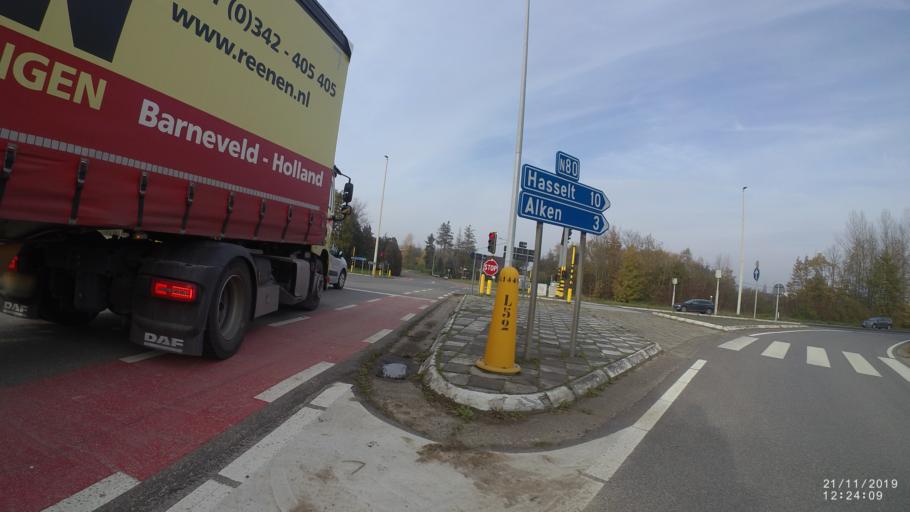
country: BE
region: Flanders
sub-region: Provincie Limburg
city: Alken
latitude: 50.8636
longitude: 5.2699
